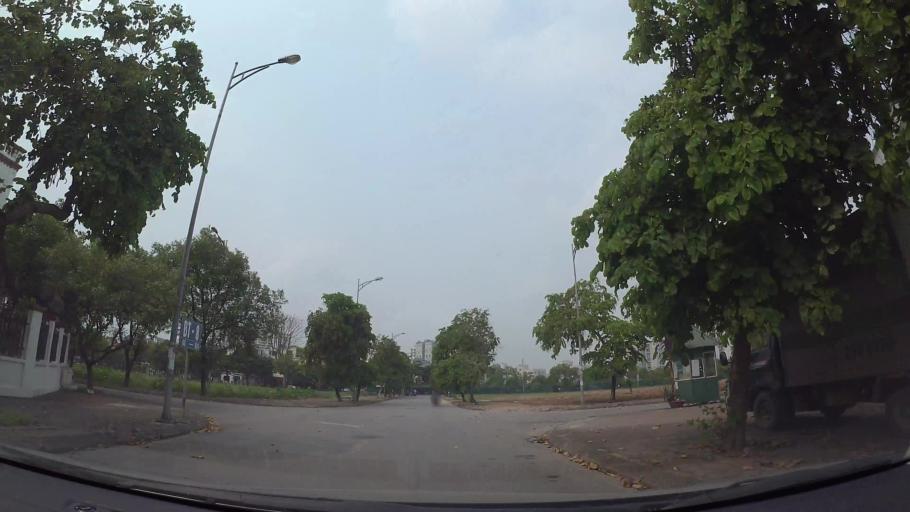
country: VN
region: Ha Noi
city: Trau Quy
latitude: 21.0587
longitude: 105.9114
